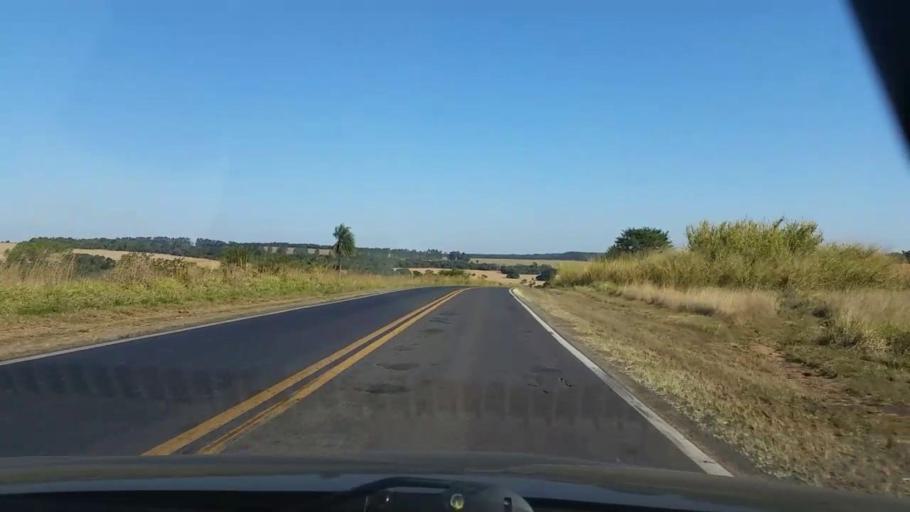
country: BR
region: Sao Paulo
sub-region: Avare
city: Avare
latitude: -22.9064
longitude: -48.7695
